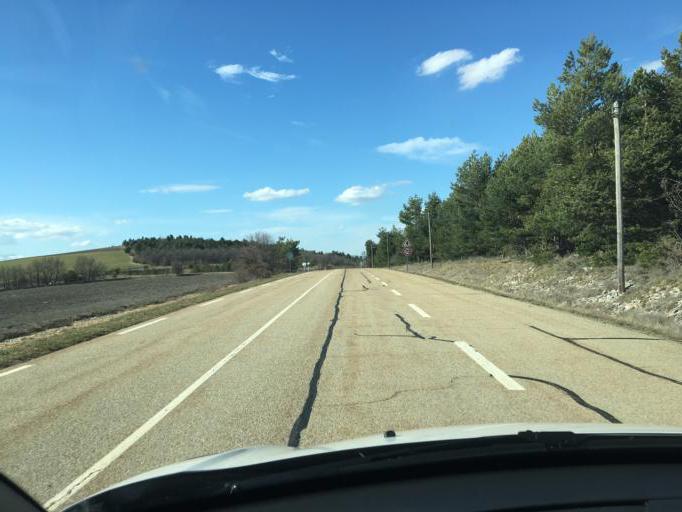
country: FR
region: Provence-Alpes-Cote d'Azur
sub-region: Departement du Vaucluse
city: Sault
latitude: 44.0268
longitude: 5.4676
